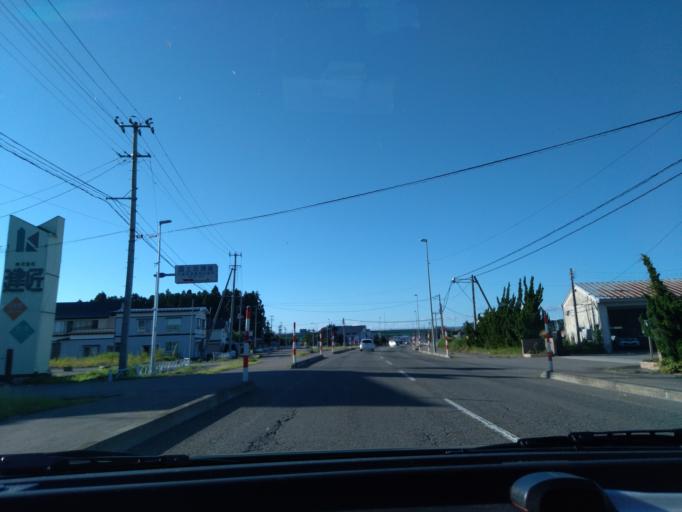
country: JP
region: Akita
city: Omagari
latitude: 39.4339
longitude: 140.4839
